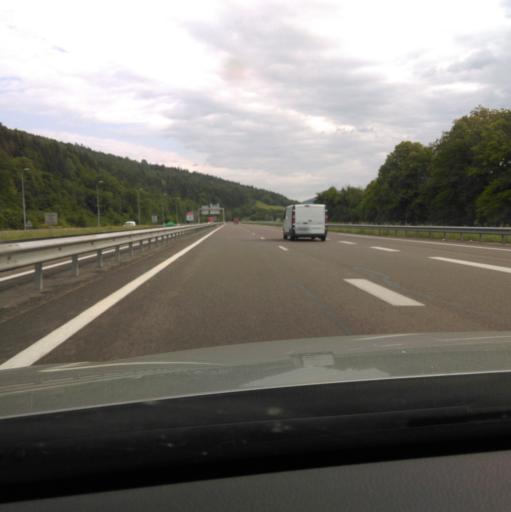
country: FR
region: Rhone-Alpes
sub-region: Departement de l'Ain
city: Saint-Martin-du-Frene
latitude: 46.1383
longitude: 5.5415
